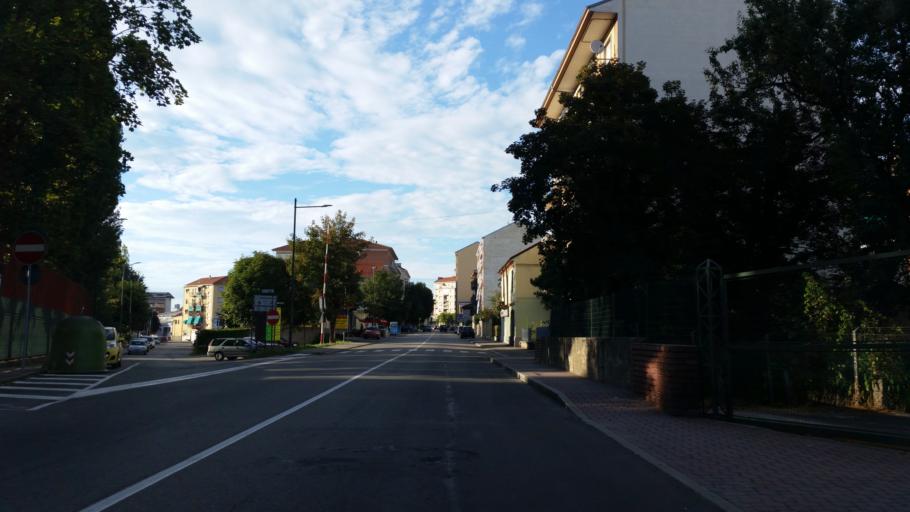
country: IT
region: Piedmont
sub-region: Provincia di Asti
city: Asti
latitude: 44.8972
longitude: 8.1934
